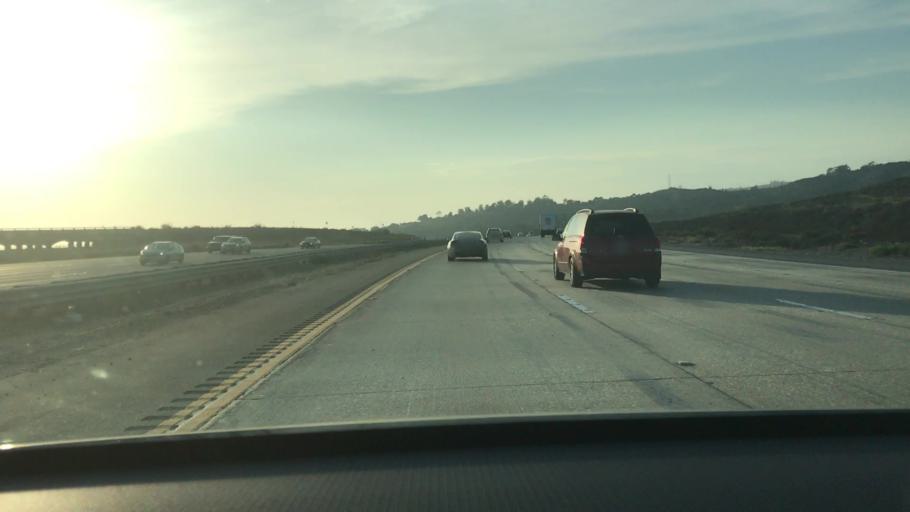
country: US
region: California
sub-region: Orange County
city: San Clemente
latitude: 33.3755
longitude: -117.5616
